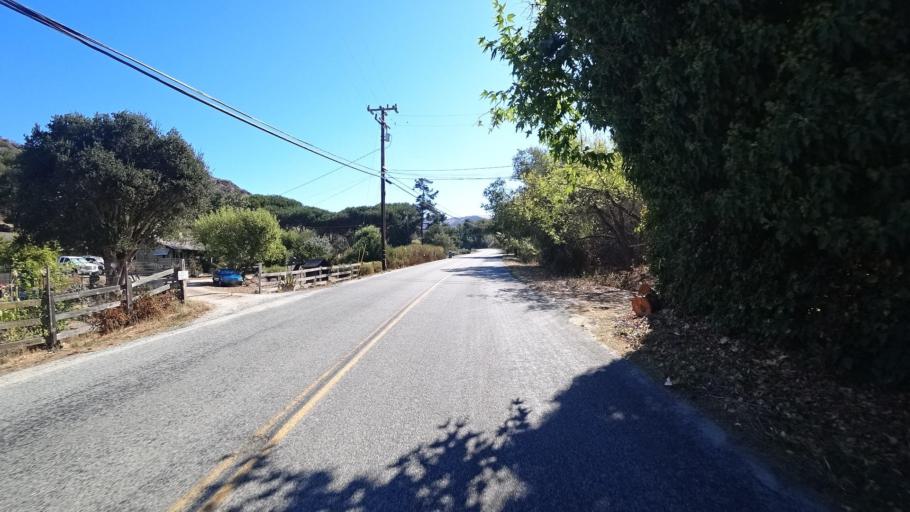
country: US
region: California
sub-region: Monterey County
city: Carmel Valley Village
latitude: 36.5507
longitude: -121.6891
